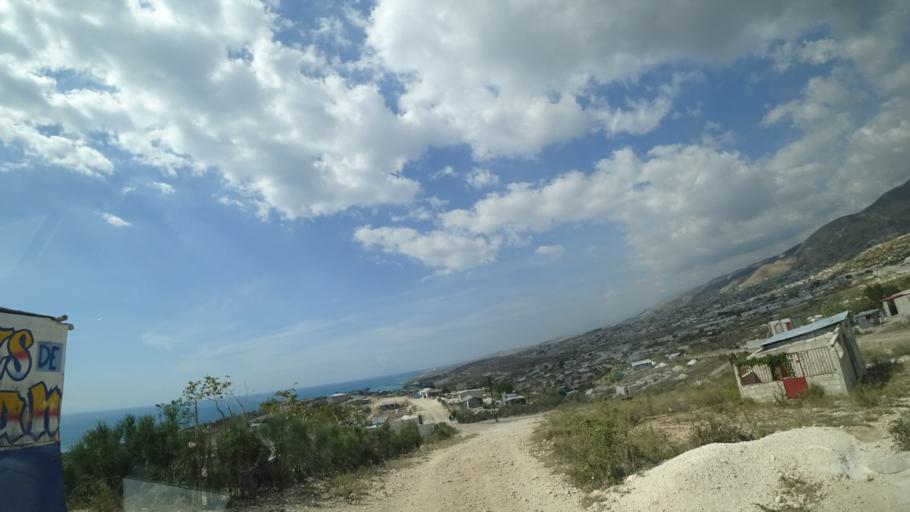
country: HT
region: Ouest
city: Cabaret
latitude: 18.6781
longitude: -72.3098
